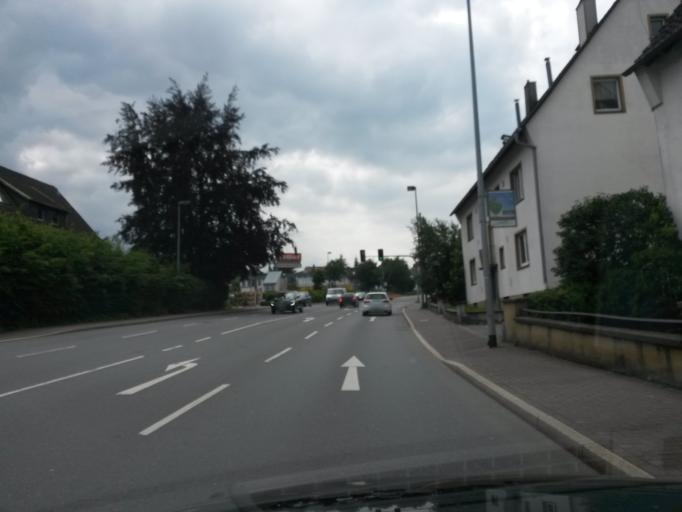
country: DE
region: North Rhine-Westphalia
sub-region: Regierungsbezirk Arnsberg
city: Luedenscheid
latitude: 51.2130
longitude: 7.6457
